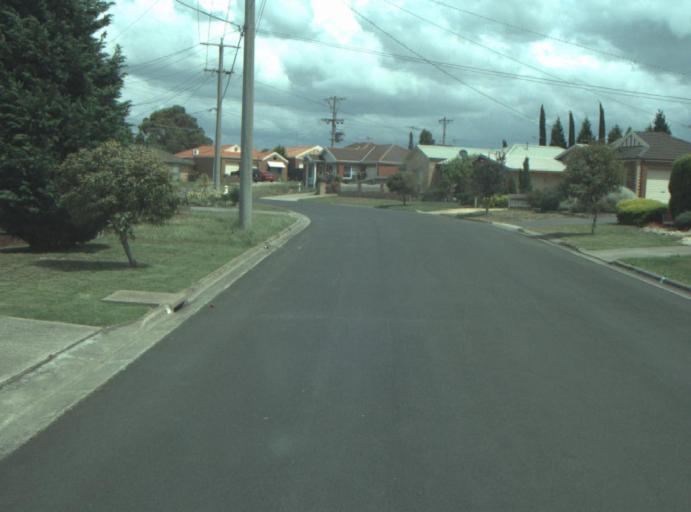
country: AU
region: Victoria
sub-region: Greater Geelong
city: Bell Park
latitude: -38.0941
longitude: 144.3413
